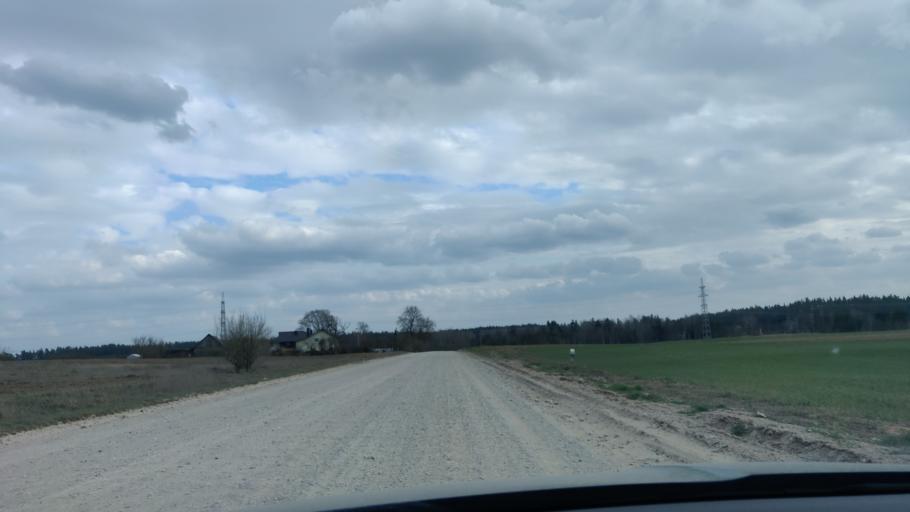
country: LT
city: Lentvaris
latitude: 54.6117
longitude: 25.0703
